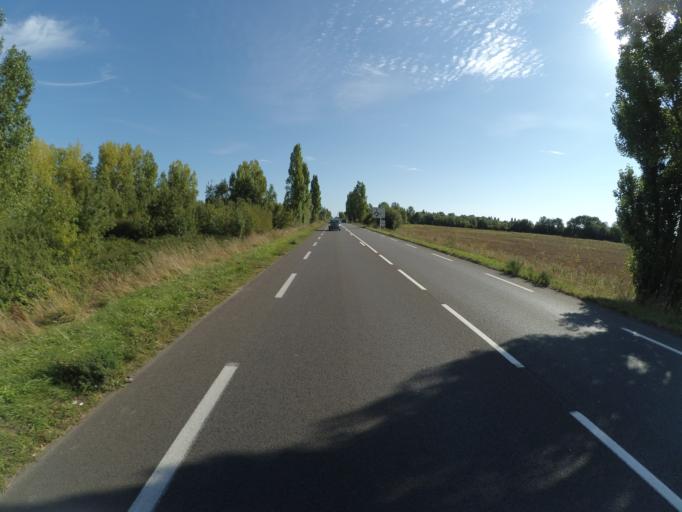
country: FR
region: Pays de la Loire
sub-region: Departement de la Vendee
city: Angles
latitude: 46.3951
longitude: -1.3990
